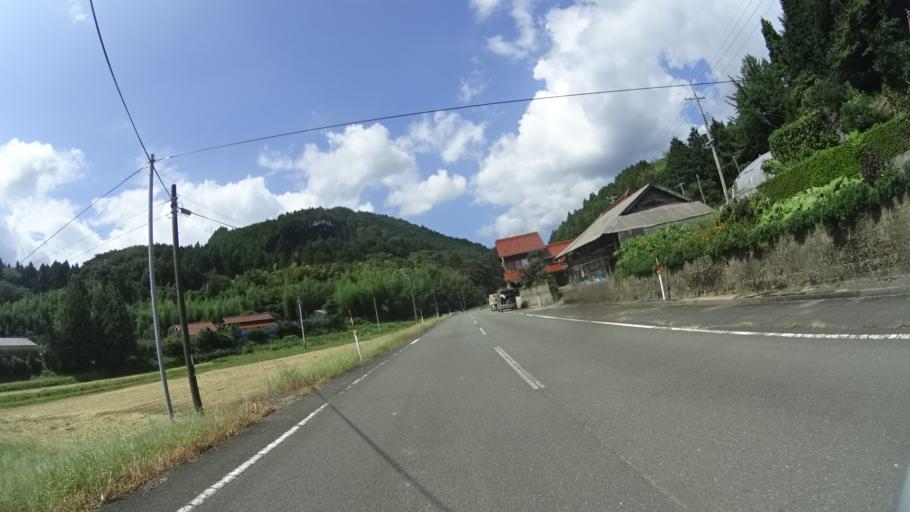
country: JP
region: Yamaguchi
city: Hagi
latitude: 34.4914
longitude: 131.5747
